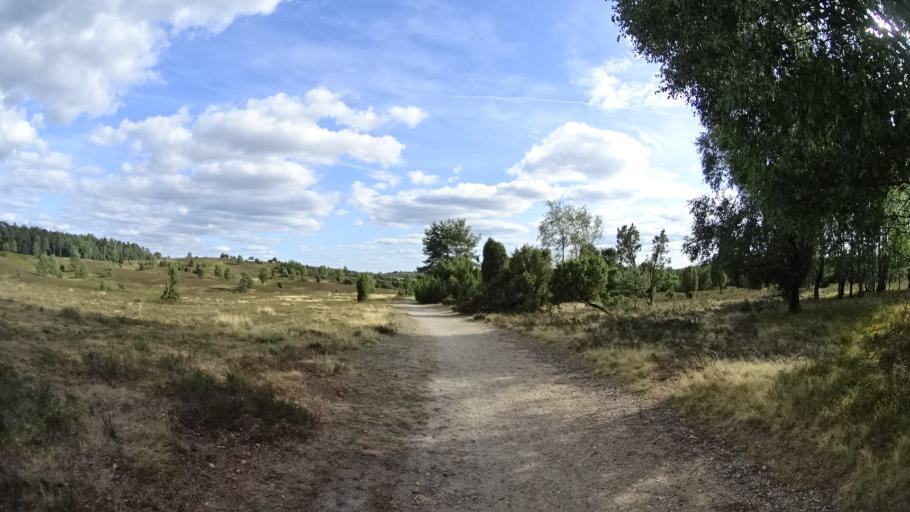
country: DE
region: Lower Saxony
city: Undeloh
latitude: 53.1605
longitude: 9.9282
